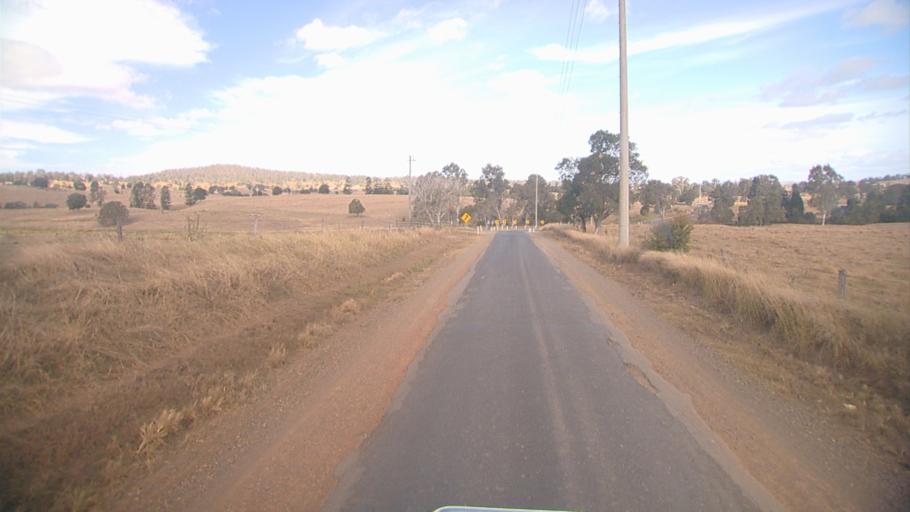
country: AU
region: Queensland
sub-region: Logan
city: Cedar Vale
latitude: -27.9106
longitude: 153.0136
